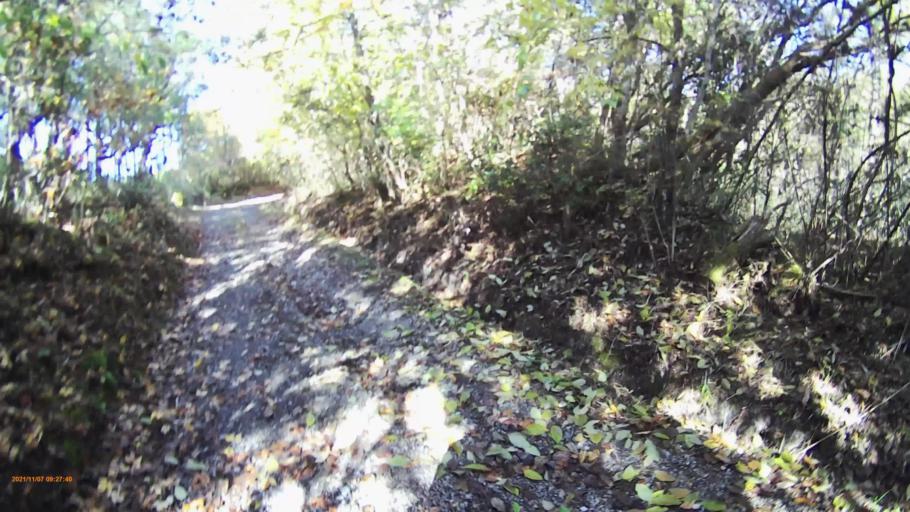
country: JP
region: Gifu
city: Mizunami
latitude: 35.4458
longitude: 137.3521
